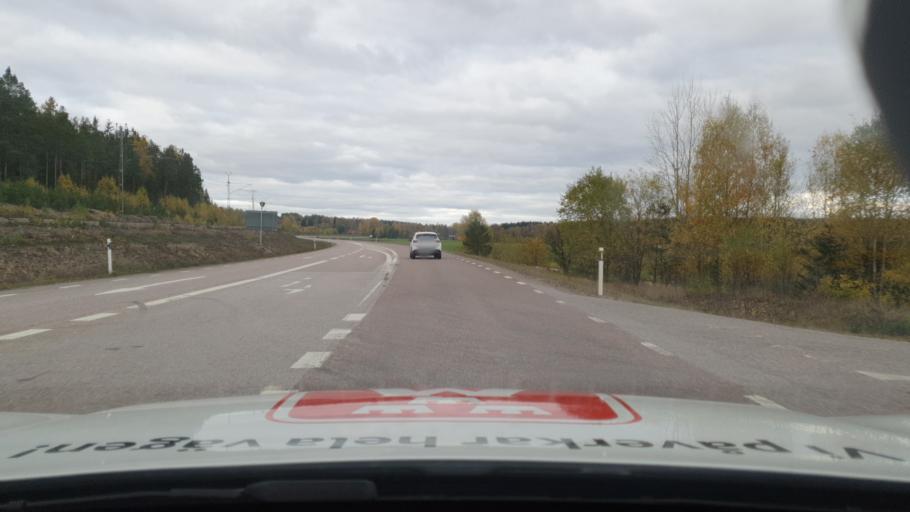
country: SE
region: Dalarna
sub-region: Avesta Kommun
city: Horndal
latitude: 60.2719
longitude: 16.4047
